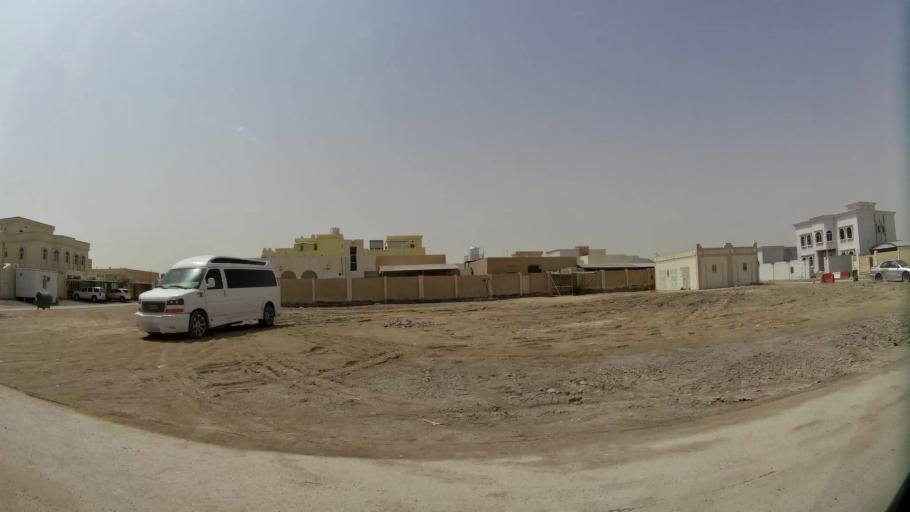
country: QA
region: Baladiyat ar Rayyan
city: Ar Rayyan
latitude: 25.2331
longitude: 51.4197
